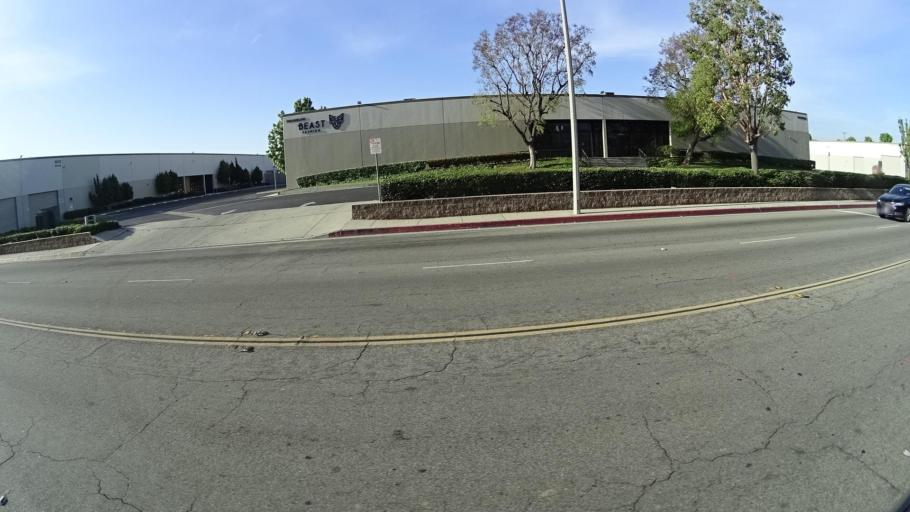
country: US
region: California
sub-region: Los Angeles County
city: South San Jose Hills
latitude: 34.0010
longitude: -117.9094
